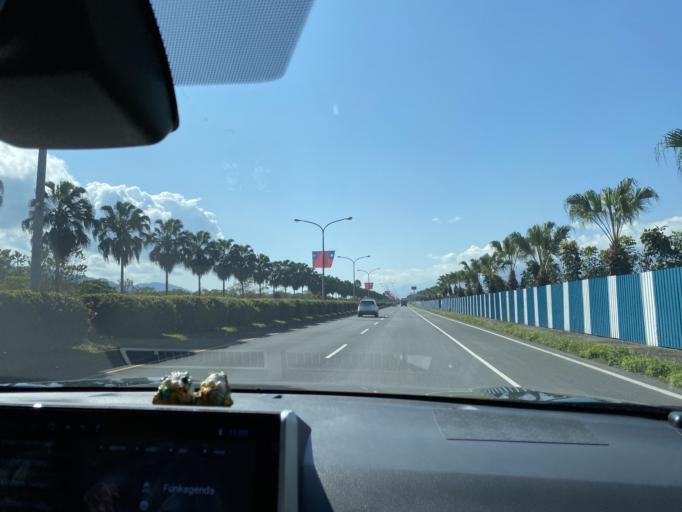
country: TW
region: Taiwan
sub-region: Hualien
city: Hualian
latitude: 23.8695
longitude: 121.5346
